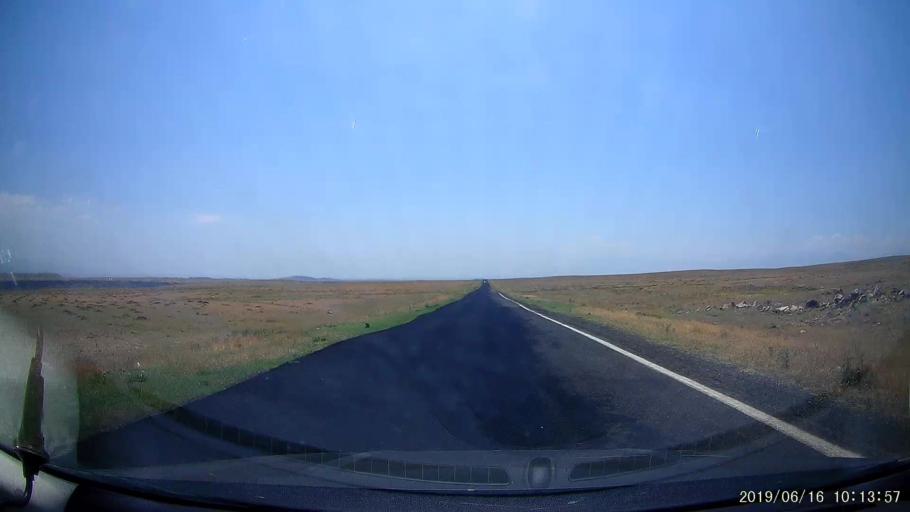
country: TR
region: Igdir
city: Tuzluca
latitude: 40.1891
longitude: 43.6528
